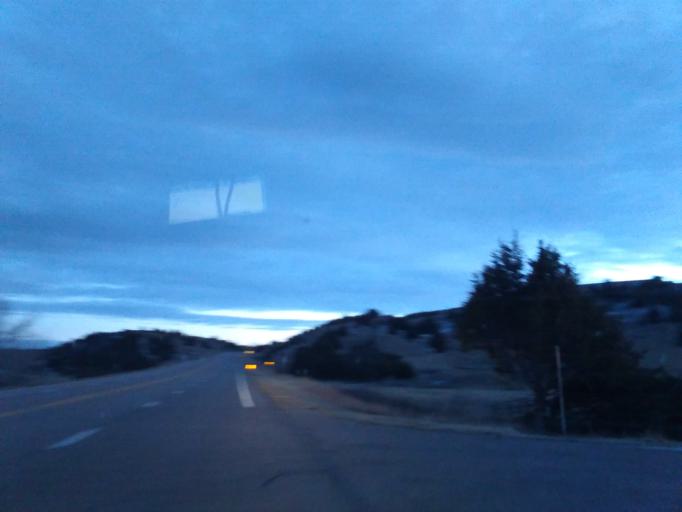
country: US
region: Nebraska
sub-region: Garden County
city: Oshkosh
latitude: 41.2651
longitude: -102.1105
